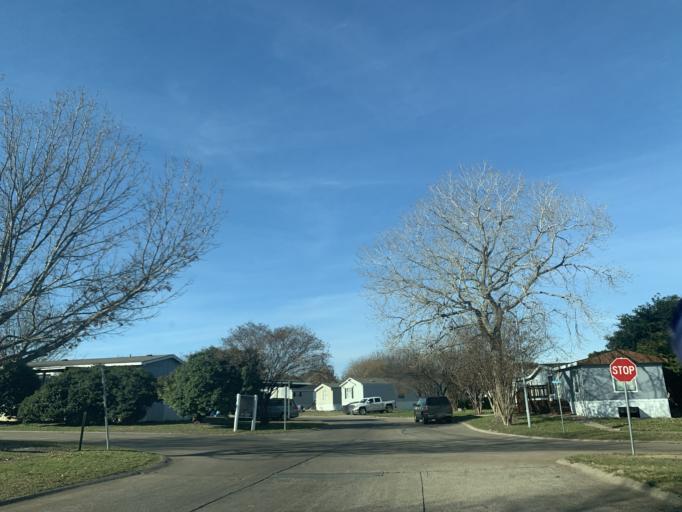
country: US
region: Texas
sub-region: Dallas County
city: DeSoto
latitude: 32.5734
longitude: -96.8239
